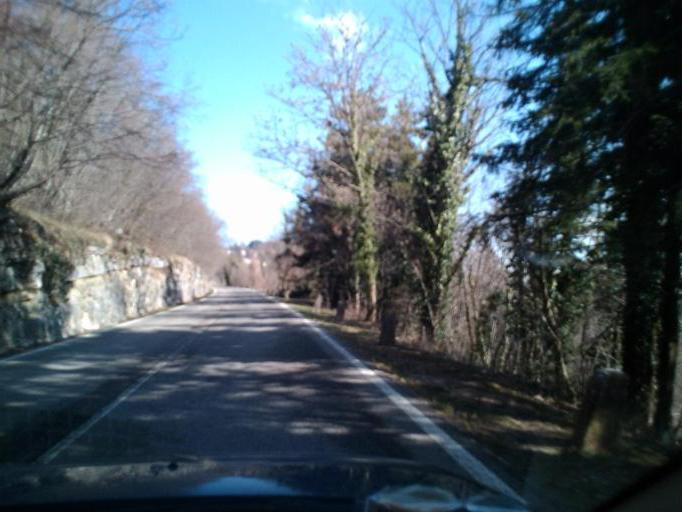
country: IT
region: Veneto
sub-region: Provincia di Verona
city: Bosco Chiesanuova
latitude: 45.6123
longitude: 11.0303
